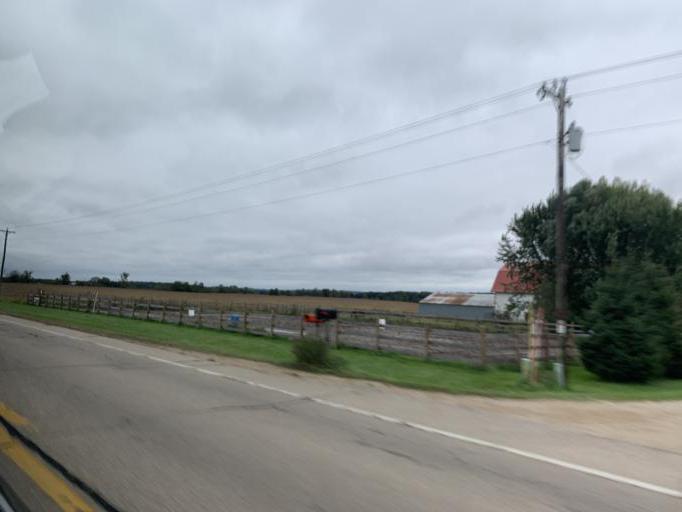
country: US
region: Wisconsin
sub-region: Grant County
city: Muscoda
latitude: 43.2198
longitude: -90.5226
